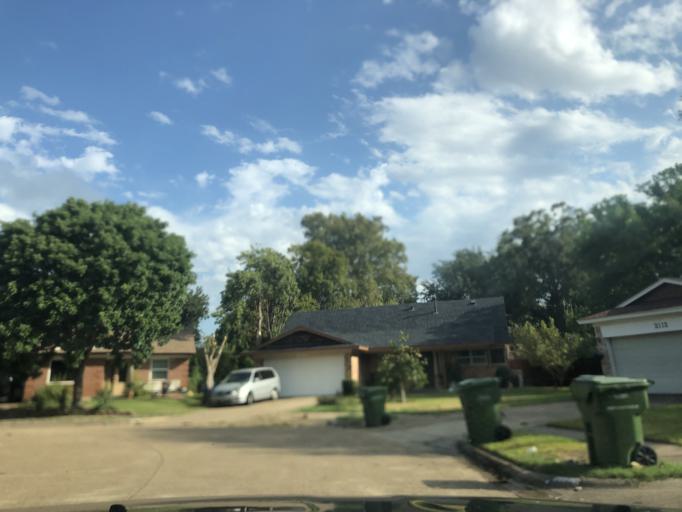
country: US
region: Texas
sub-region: Dallas County
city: Garland
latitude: 32.8855
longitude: -96.6583
